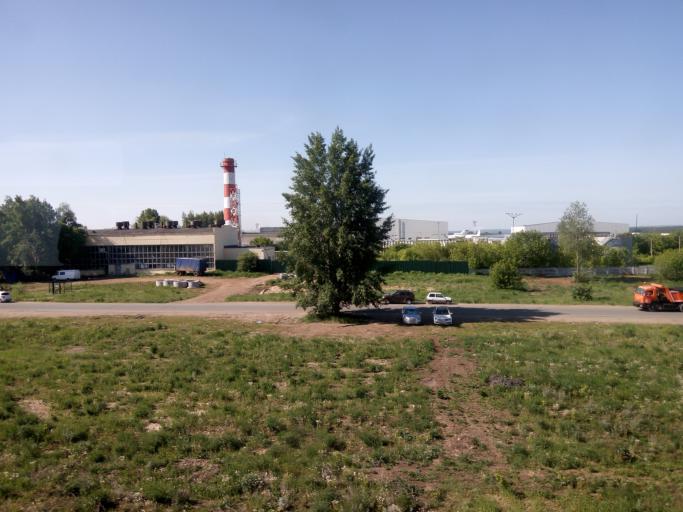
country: RU
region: Tatarstan
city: Stolbishchi
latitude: 55.6161
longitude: 49.2815
